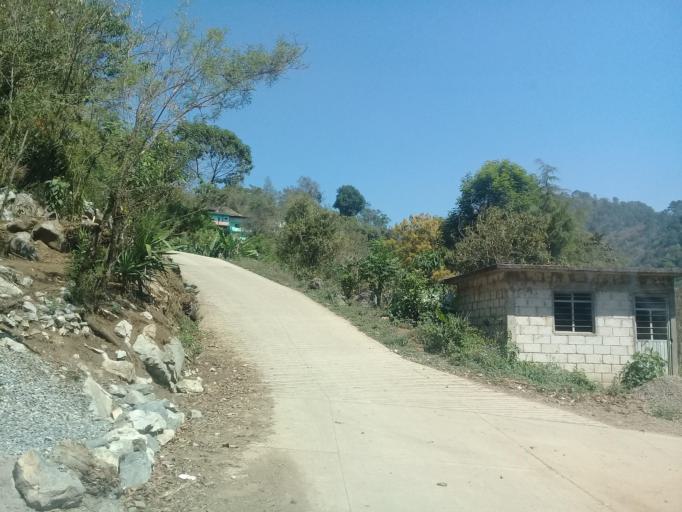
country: MX
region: Veracruz
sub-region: Tlilapan
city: Tonalixco
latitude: 18.7591
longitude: -97.0447
